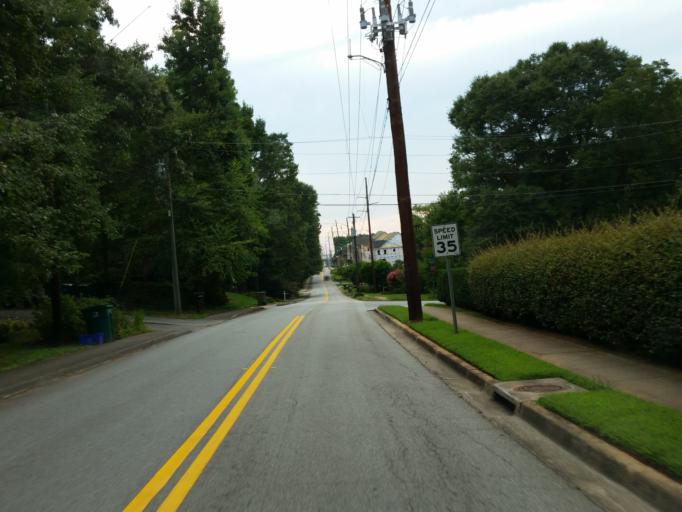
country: US
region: Georgia
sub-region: Cobb County
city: Smyrna
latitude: 33.8906
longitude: -84.5103
